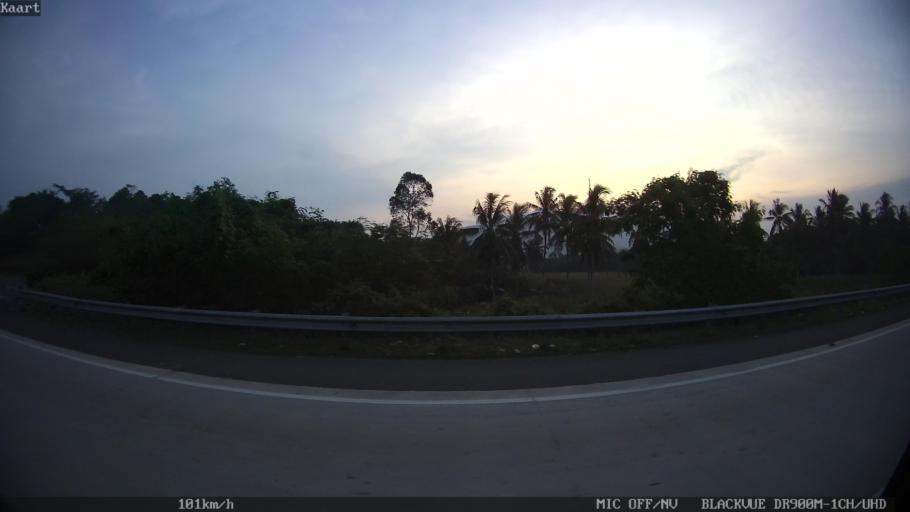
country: ID
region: Lampung
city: Penengahan
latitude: -5.7789
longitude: 105.7200
